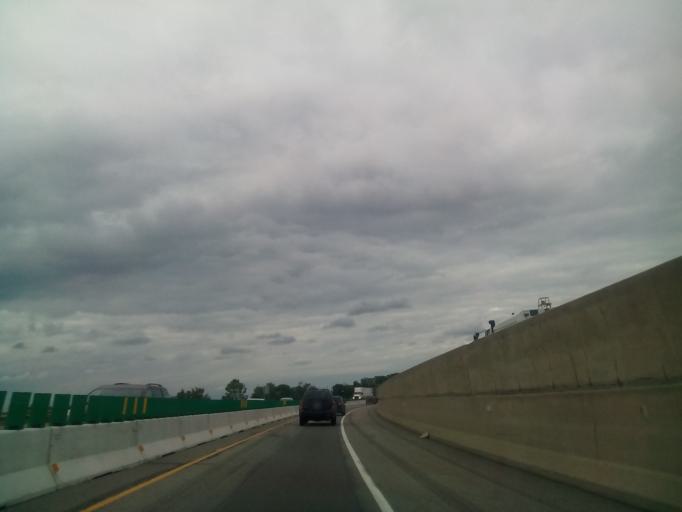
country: US
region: Ohio
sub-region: Lorain County
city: Elyria
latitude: 41.3919
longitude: -82.1242
